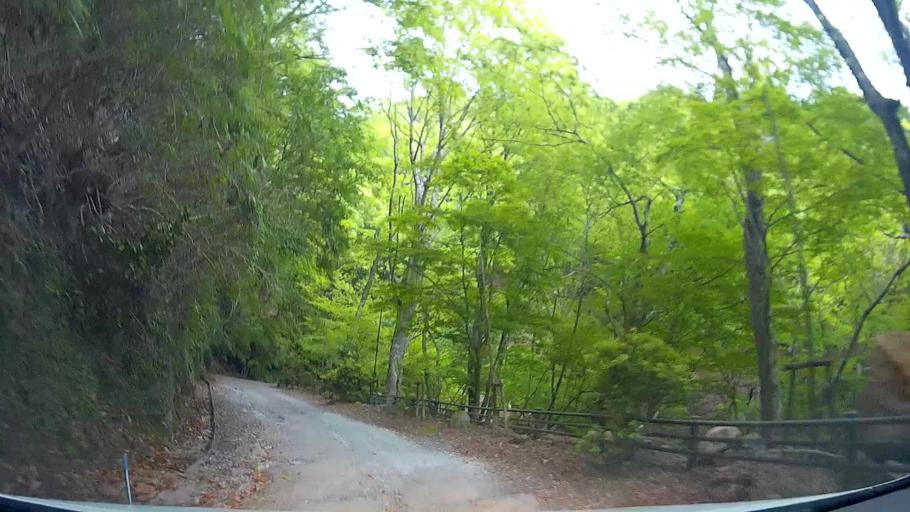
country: JP
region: Shizuoka
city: Shimoda
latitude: 34.8340
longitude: 138.9329
